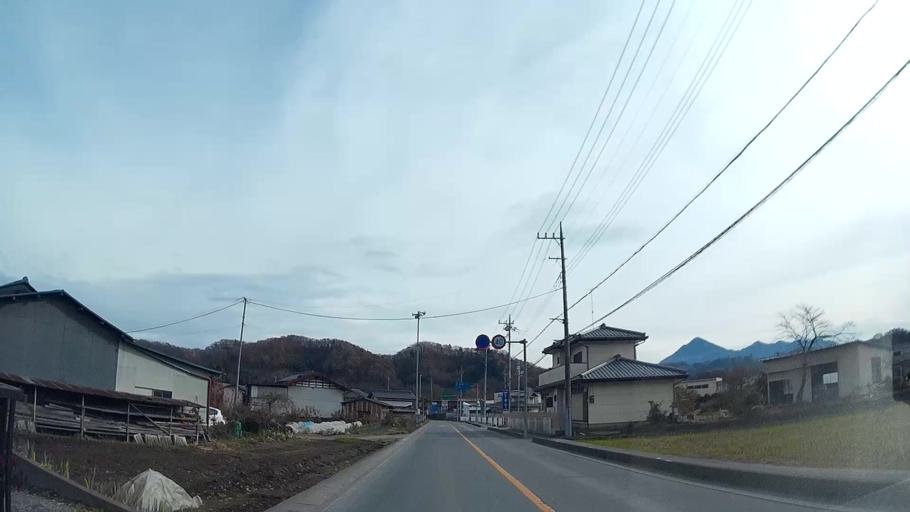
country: JP
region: Saitama
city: Chichibu
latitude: 36.0142
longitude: 139.0364
